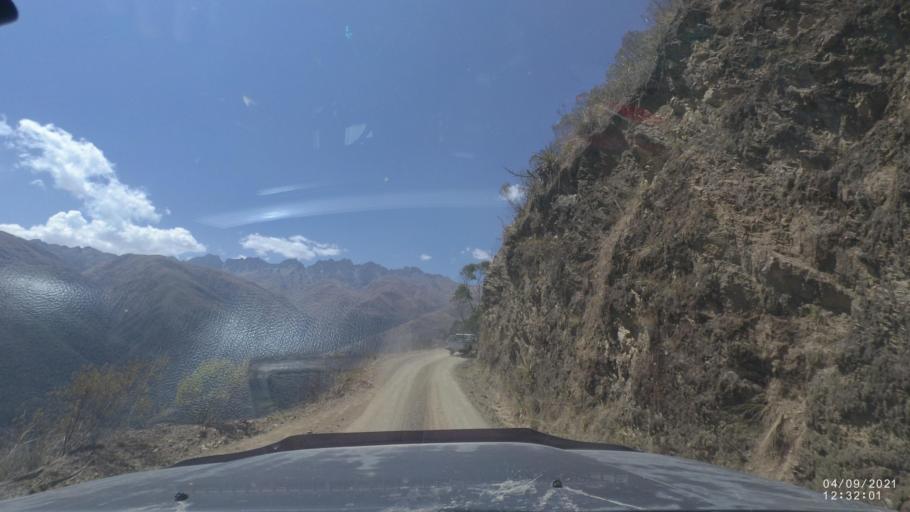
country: BO
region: Cochabamba
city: Colchani
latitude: -17.2242
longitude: -66.5216
